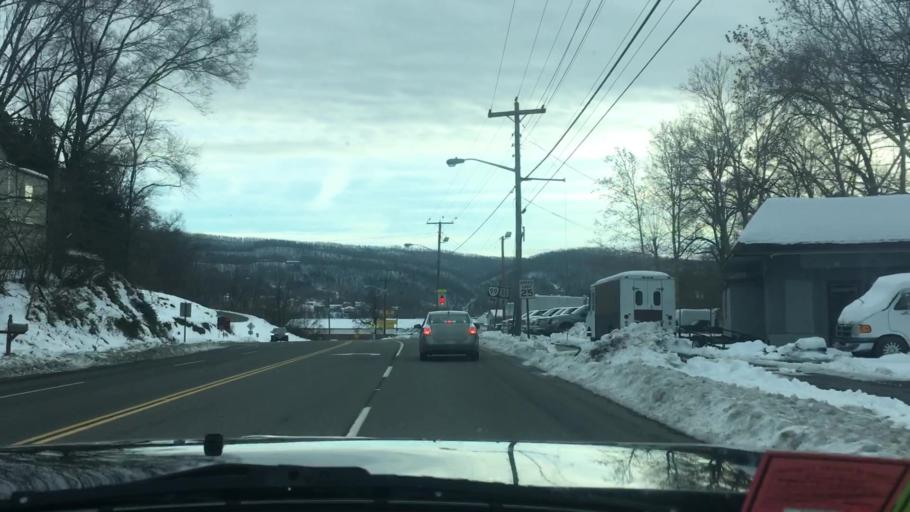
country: US
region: Virginia
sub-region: Pulaski County
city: Pulaski
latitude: 37.0536
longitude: -80.7741
